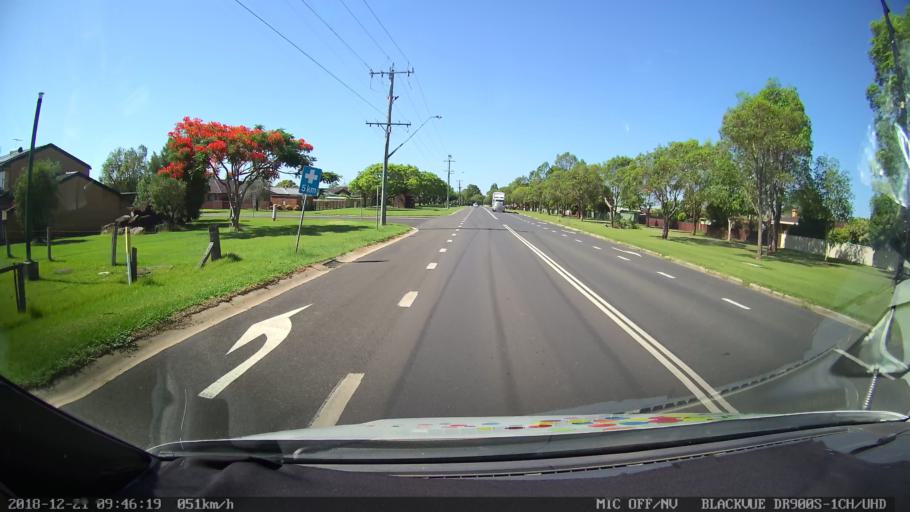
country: AU
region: New South Wales
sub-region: Clarence Valley
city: Grafton
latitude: -29.6375
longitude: 152.9264
